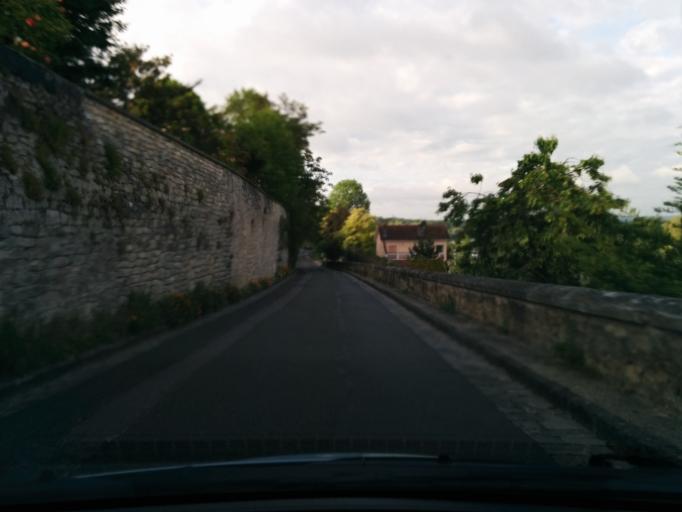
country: FR
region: Ile-de-France
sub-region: Departement des Yvelines
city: Follainville-Dennemont
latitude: 49.0608
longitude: 1.7009
